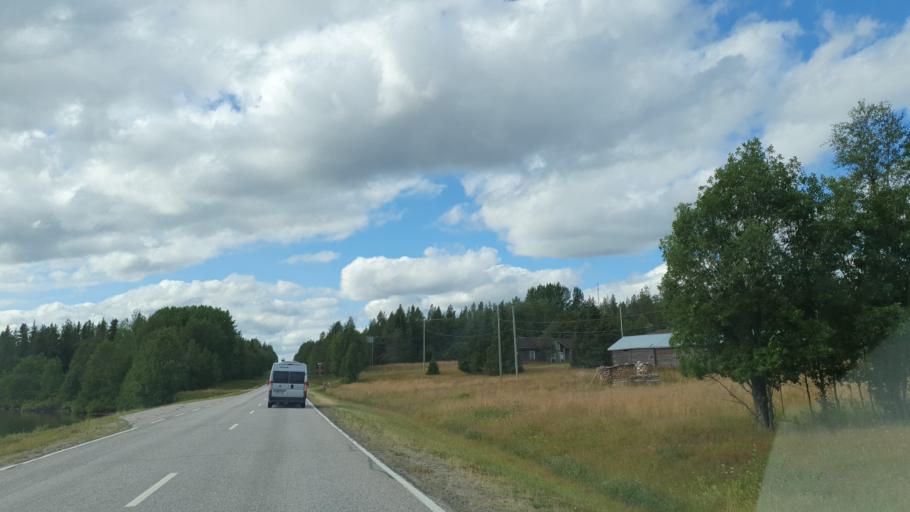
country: FI
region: Lapland
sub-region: Tunturi-Lappi
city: Muonio
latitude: 67.8610
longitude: 24.1219
